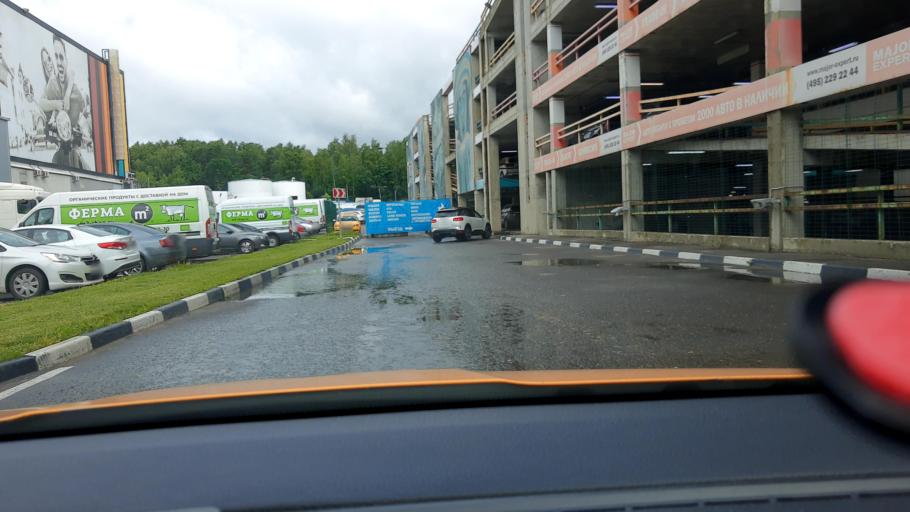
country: RU
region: Moskovskaya
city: Opalikha
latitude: 55.7902
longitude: 37.2535
